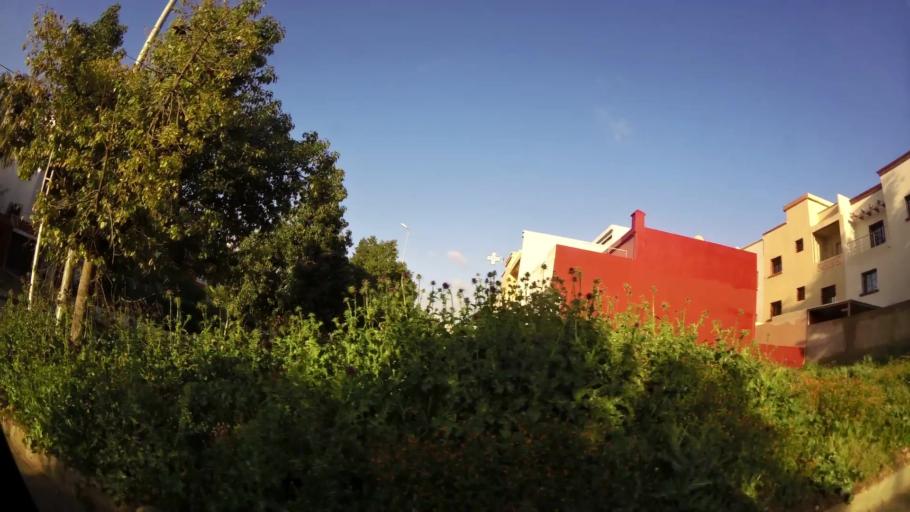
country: MA
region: Chaouia-Ouardigha
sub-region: Settat Province
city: Settat
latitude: 33.0103
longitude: -7.6132
